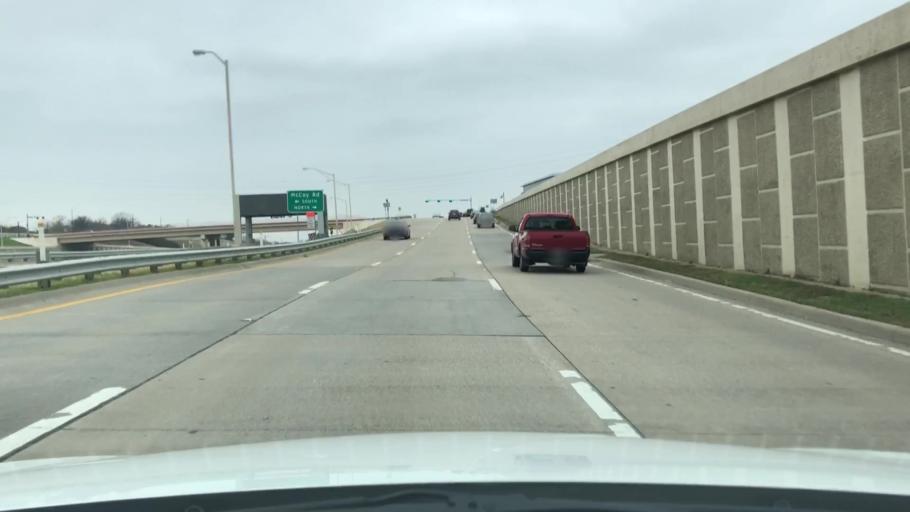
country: US
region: Texas
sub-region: Dallas County
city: Carrollton
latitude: 32.9855
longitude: -96.8947
